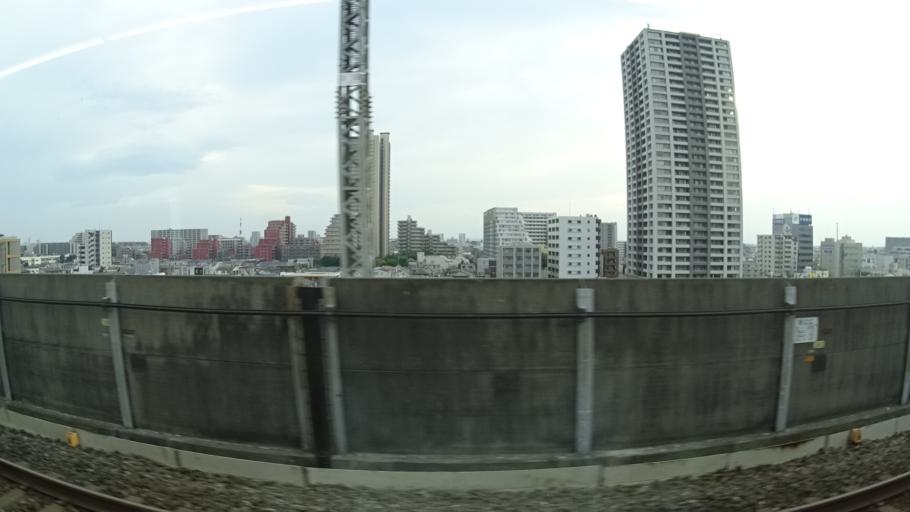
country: JP
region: Saitama
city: Yono
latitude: 35.8983
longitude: 139.6283
